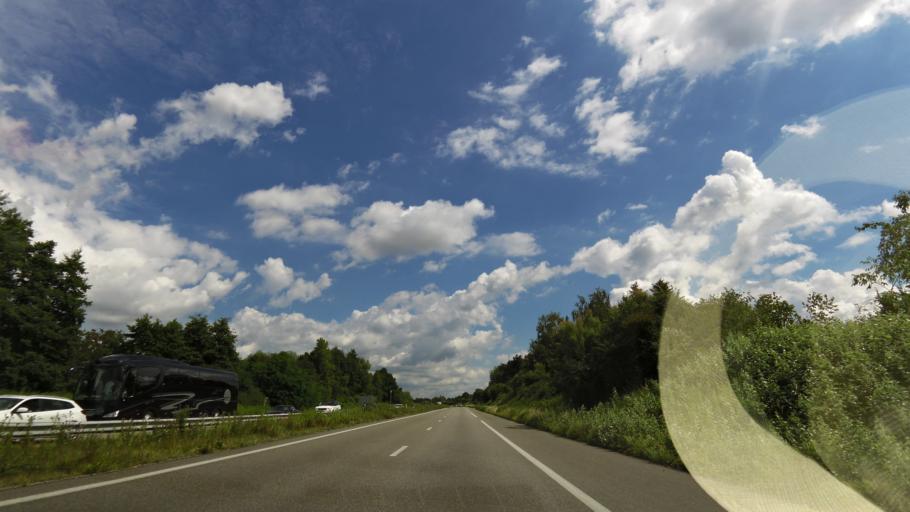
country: FR
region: Alsace
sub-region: Departement du Bas-Rhin
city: Herrlisheim
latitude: 48.7308
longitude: 7.8928
